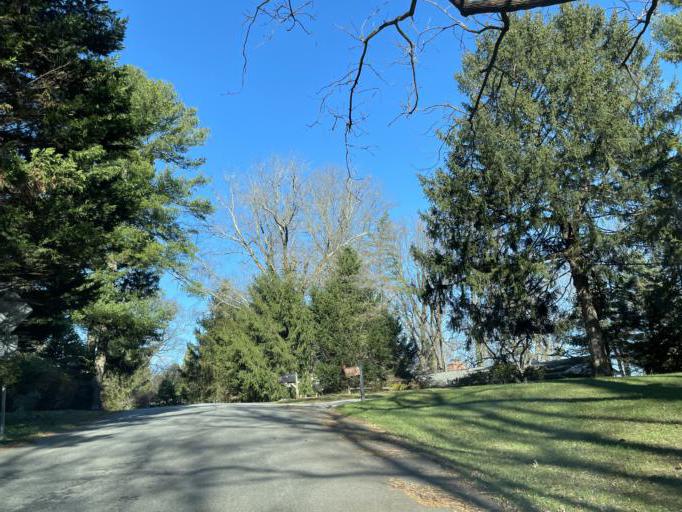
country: US
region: Maryland
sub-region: Baltimore County
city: Mays Chapel
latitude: 39.3945
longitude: -76.6565
